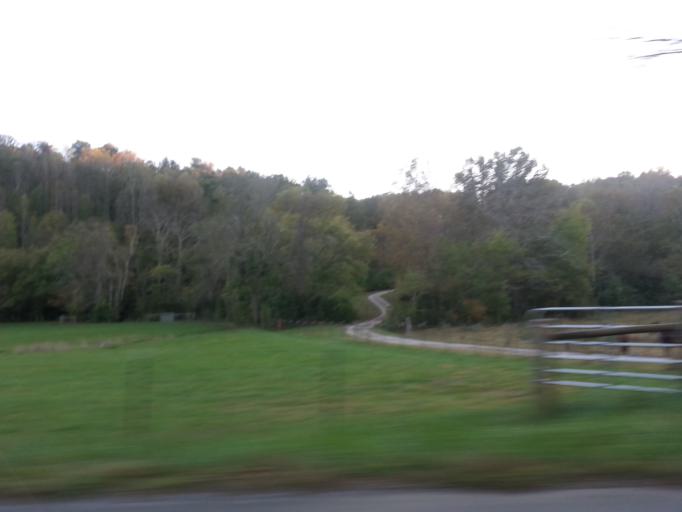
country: US
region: Tennessee
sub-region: Sevier County
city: Seymour
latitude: 35.7867
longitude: -83.7603
